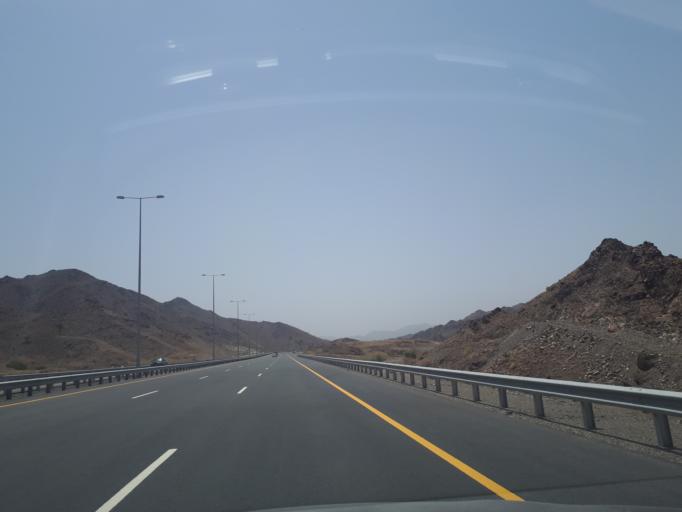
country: OM
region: Ash Sharqiyah
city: Ibra'
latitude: 22.8864
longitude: 58.2914
